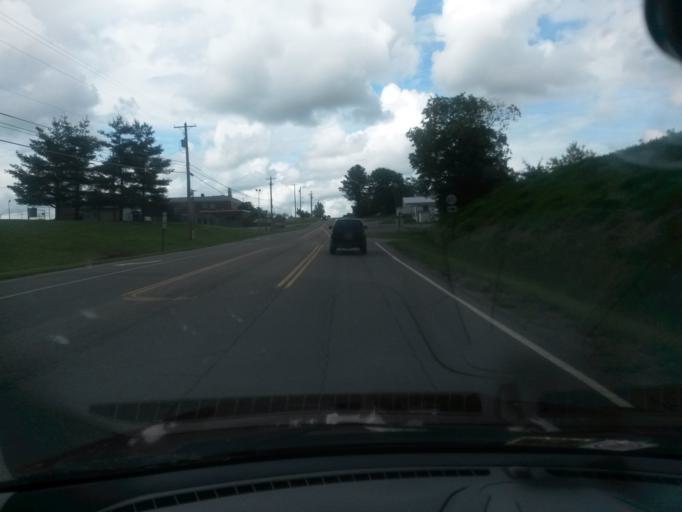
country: US
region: Virginia
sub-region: Montgomery County
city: Christiansburg
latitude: 37.0590
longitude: -80.4413
